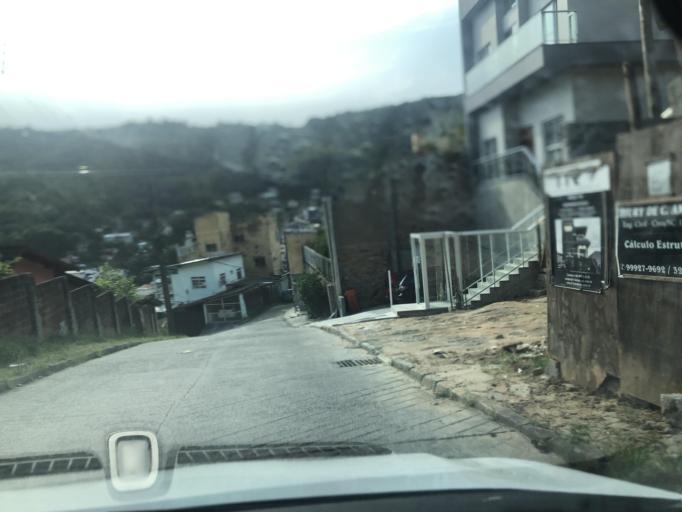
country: BR
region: Santa Catarina
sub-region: Florianopolis
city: Saco dos Limoes
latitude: -27.6034
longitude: -48.5342
